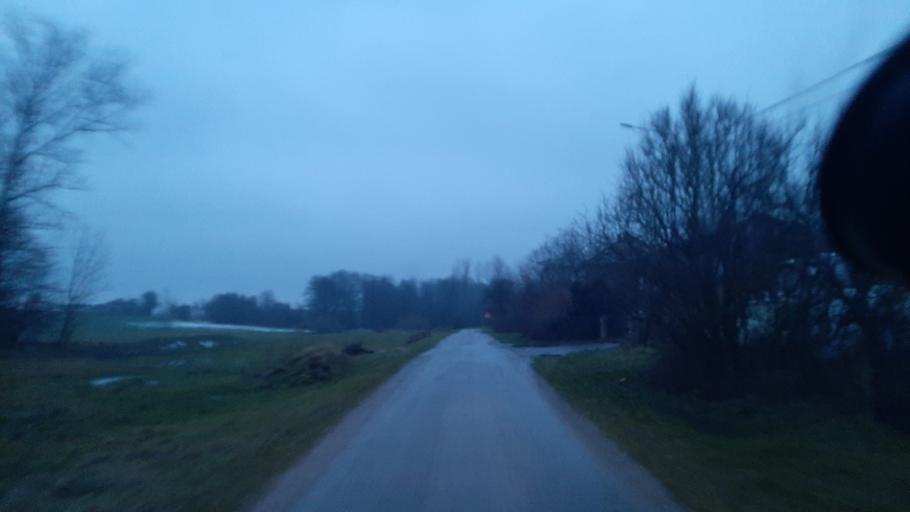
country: PL
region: Lublin Voivodeship
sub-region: Powiat lubelski
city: Jastkow
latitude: 51.3873
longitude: 22.4147
